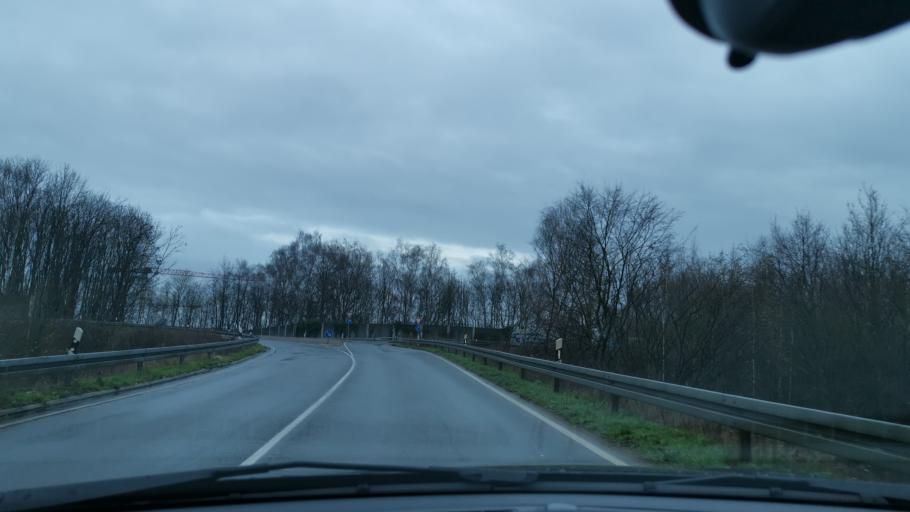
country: DE
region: North Rhine-Westphalia
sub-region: Regierungsbezirk Koln
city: Bedburg
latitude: 51.0008
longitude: 6.5659
